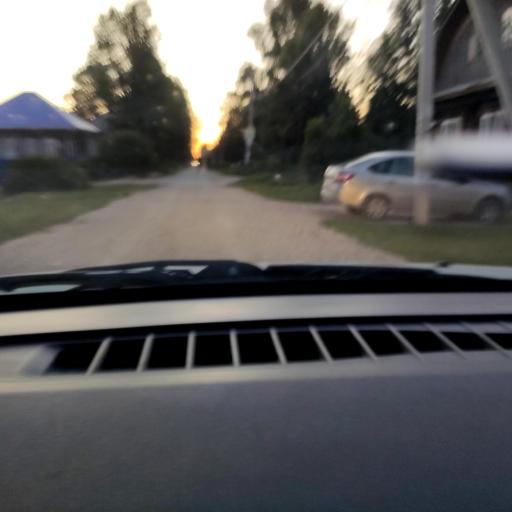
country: RU
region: Perm
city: Perm
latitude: 58.0234
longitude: 56.3268
